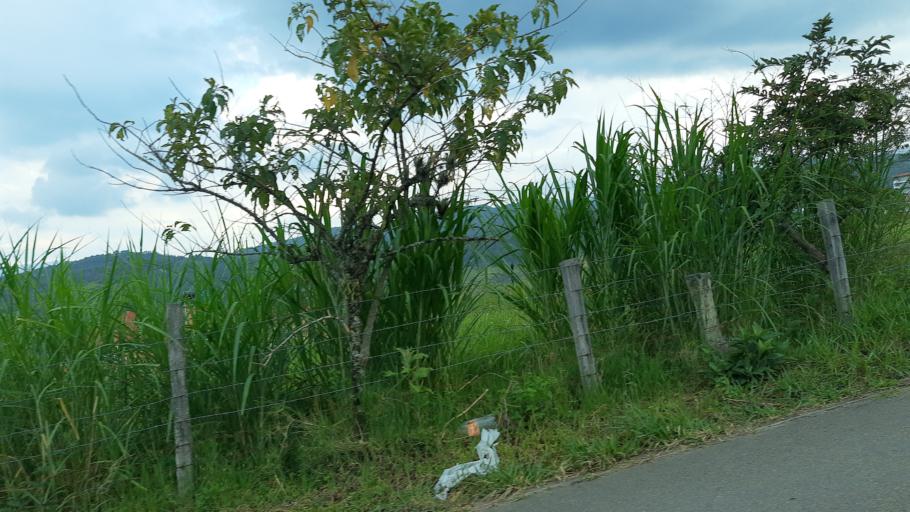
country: CO
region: Boyaca
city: Moniquira
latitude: 5.8599
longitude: -73.5769
